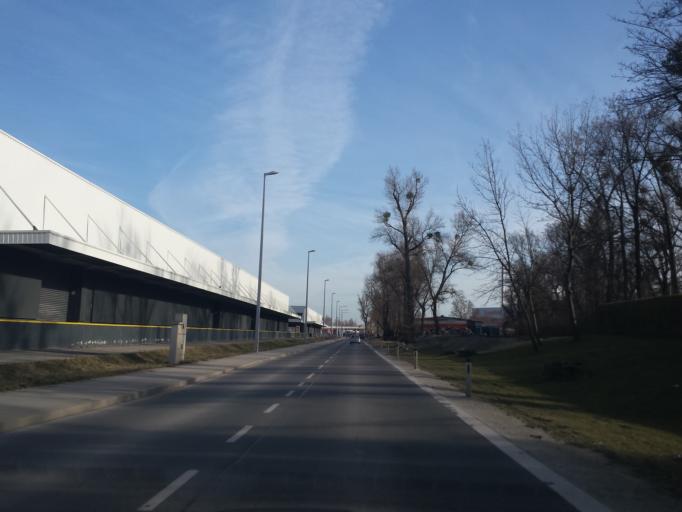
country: AT
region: Lower Austria
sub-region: Politischer Bezirk Wien-Umgebung
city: Schwechat
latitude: 48.1815
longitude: 16.4589
